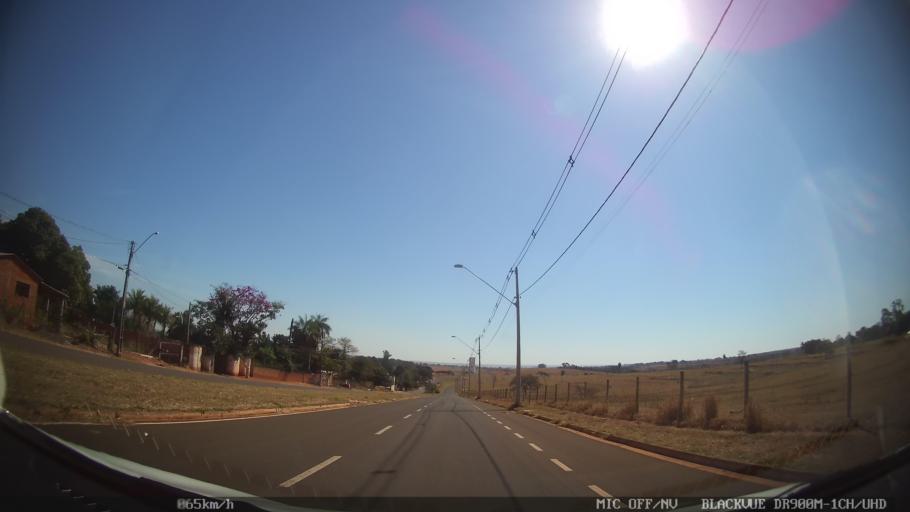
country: BR
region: Sao Paulo
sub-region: Sao Jose Do Rio Preto
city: Sao Jose do Rio Preto
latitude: -20.7306
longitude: -49.4375
